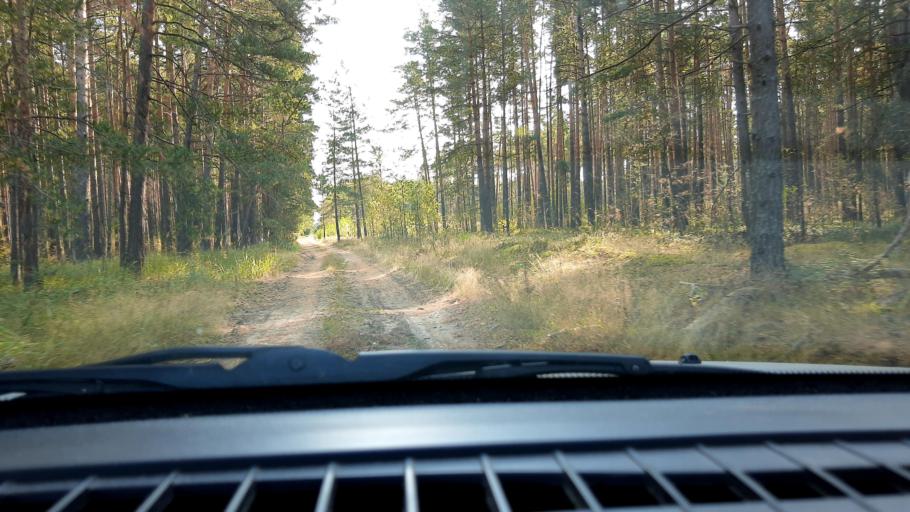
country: RU
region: Nizjnij Novgorod
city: Lukino
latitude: 56.4046
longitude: 43.6349
